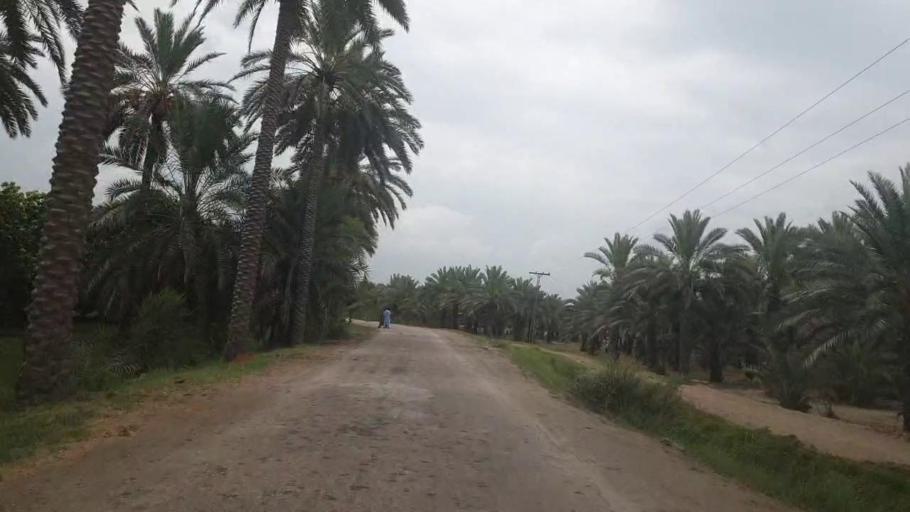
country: PK
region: Sindh
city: Khairpur
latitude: 27.5694
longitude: 68.7032
